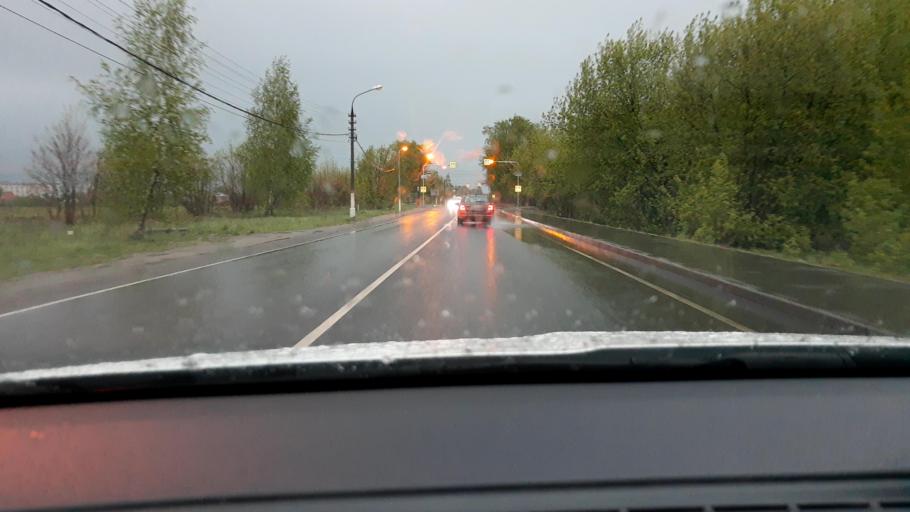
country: RU
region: Moskovskaya
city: Zagoryanskiy
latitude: 55.9286
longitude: 37.9429
